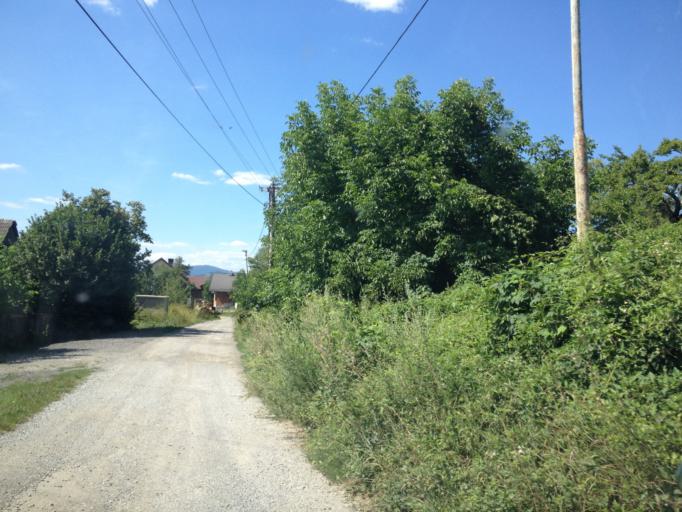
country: SK
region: Nitriansky
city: Puchov
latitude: 49.0574
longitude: 18.3495
